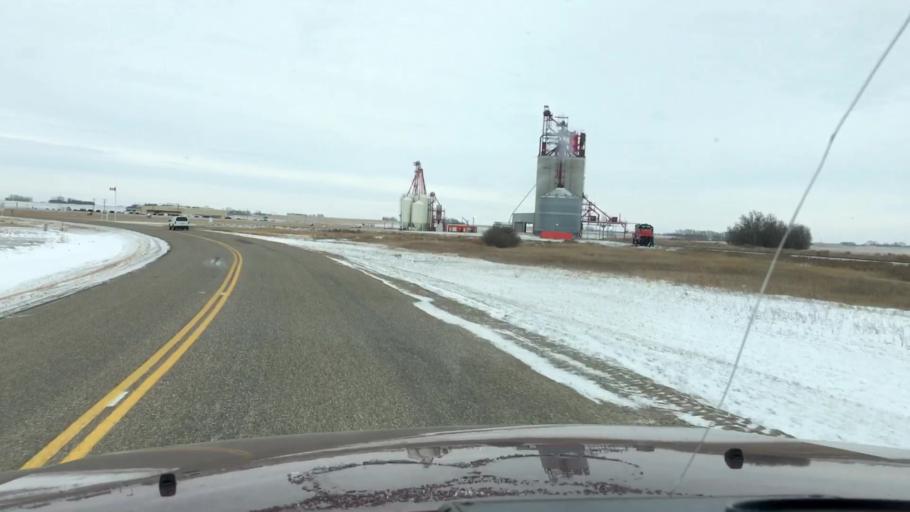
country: CA
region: Saskatchewan
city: Watrous
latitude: 51.2495
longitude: -105.9765
